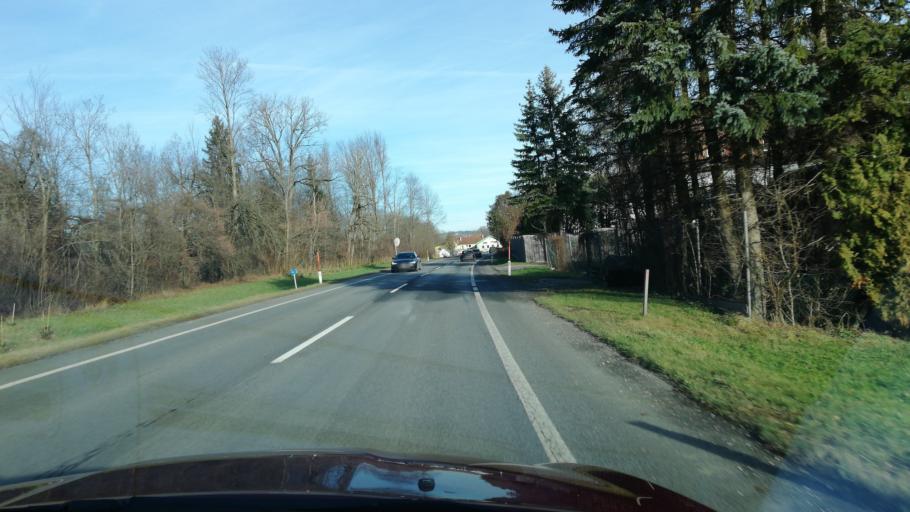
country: AT
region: Upper Austria
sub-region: Politischer Bezirk Kirchdorf an der Krems
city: Micheldorf in Oberoesterreich
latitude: 47.9396
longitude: 14.0871
